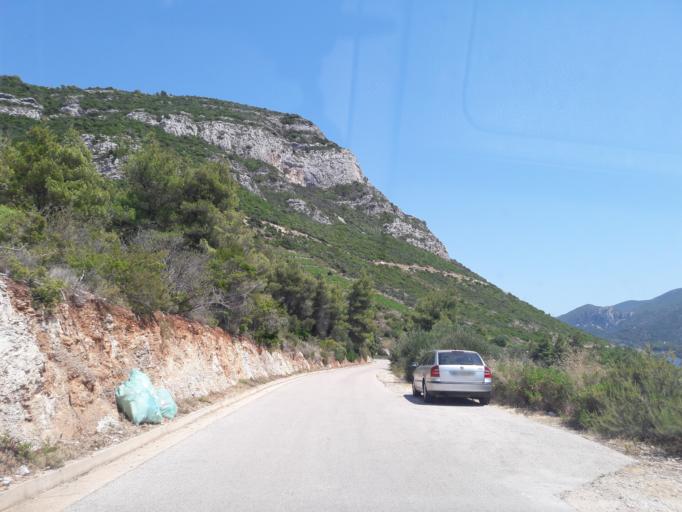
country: HR
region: Dubrovacko-Neretvanska
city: Blato
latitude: 42.9033
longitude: 17.4290
